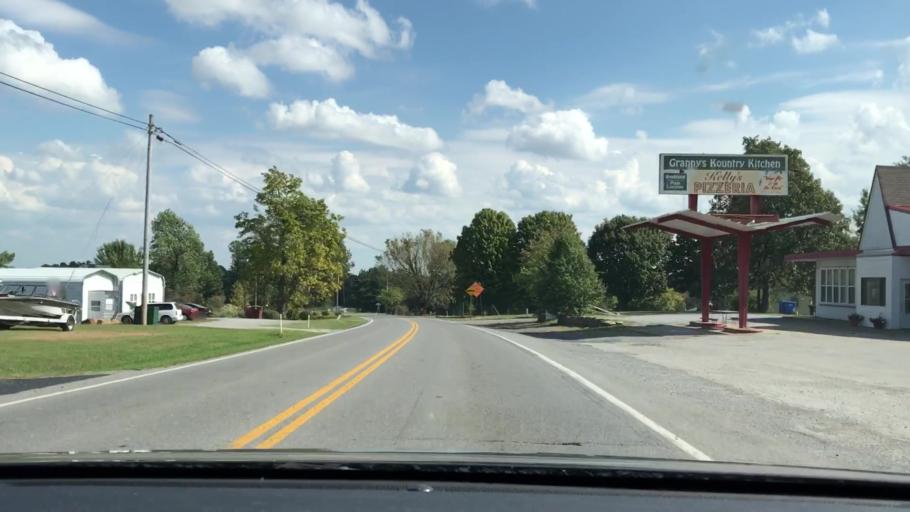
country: US
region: Kentucky
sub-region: Trigg County
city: Cadiz
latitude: 36.8112
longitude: -87.8873
